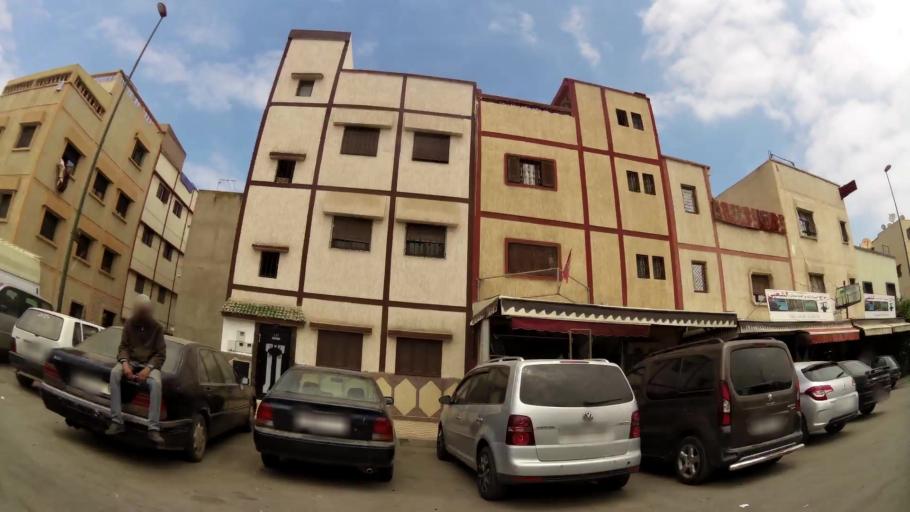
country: MA
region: Rabat-Sale-Zemmour-Zaer
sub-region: Skhirate-Temara
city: Temara
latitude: 33.9823
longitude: -6.8903
